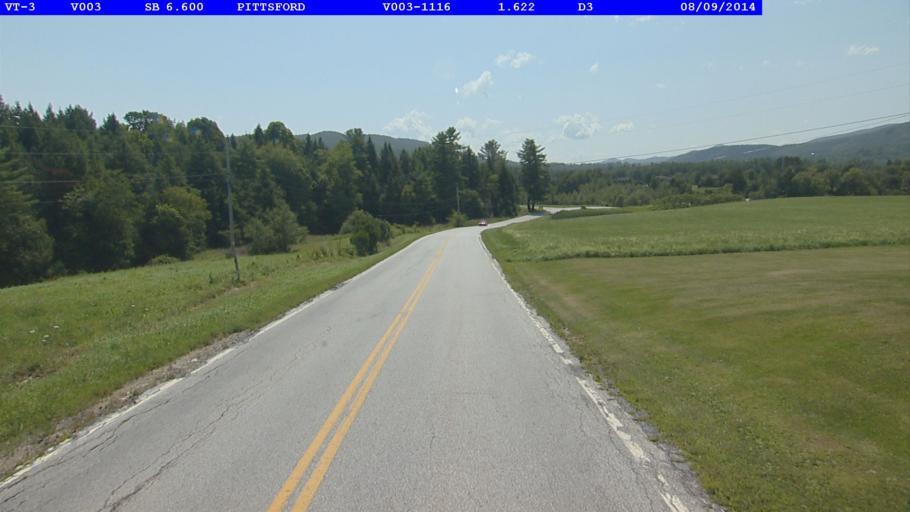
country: US
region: Vermont
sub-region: Rutland County
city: Rutland
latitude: 43.6864
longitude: -73.0209
